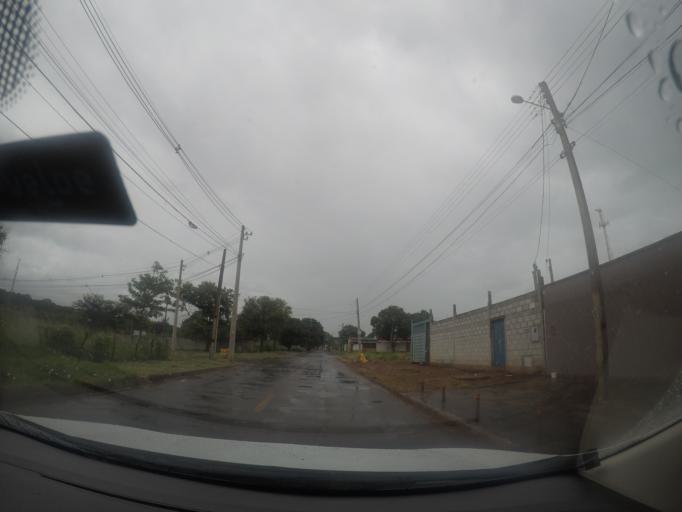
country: BR
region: Goias
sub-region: Trindade
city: Trindade
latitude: -16.6408
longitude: -49.4307
